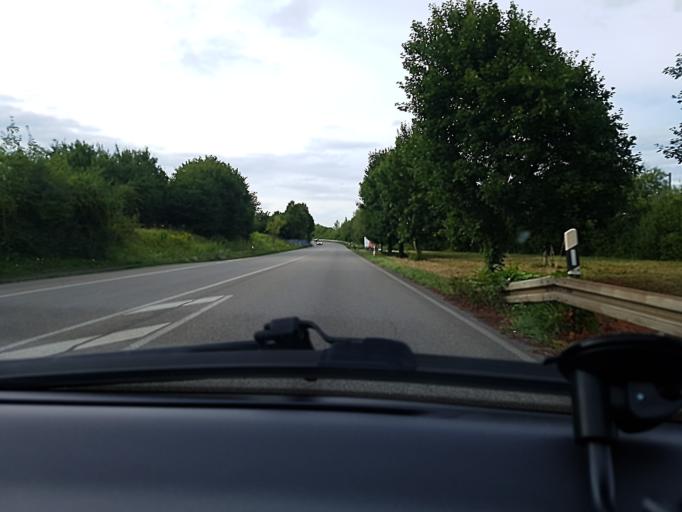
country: DE
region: Baden-Wuerttemberg
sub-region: Freiburg Region
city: Appenweier
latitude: 48.5166
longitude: 7.9648
